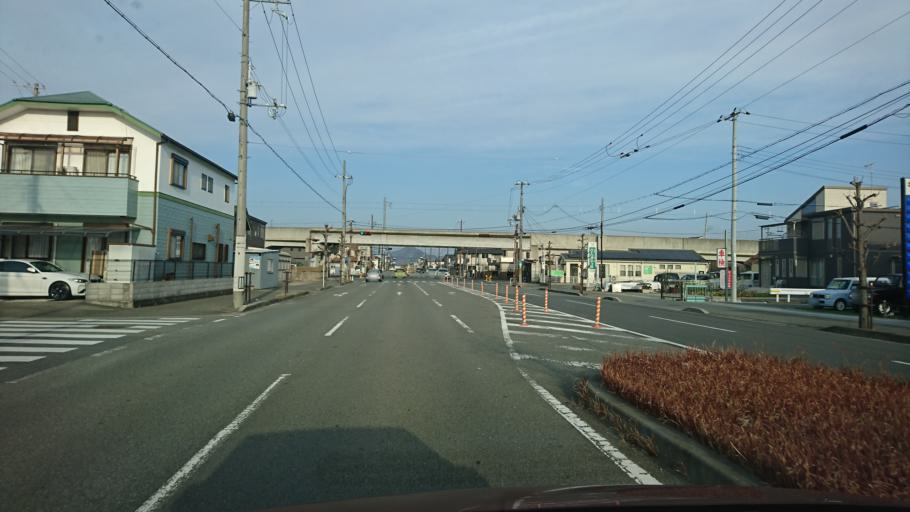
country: JP
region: Hyogo
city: Kakogawacho-honmachi
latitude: 34.7659
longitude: 134.8461
